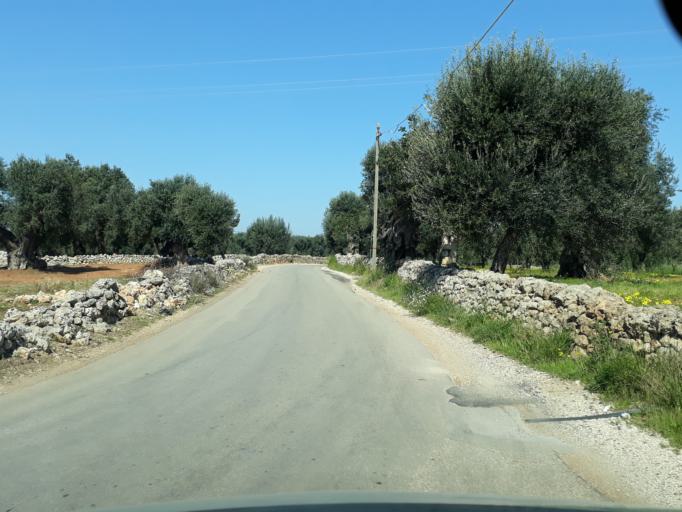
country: IT
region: Apulia
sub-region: Provincia di Brindisi
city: Fasano
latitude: 40.8302
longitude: 17.3788
